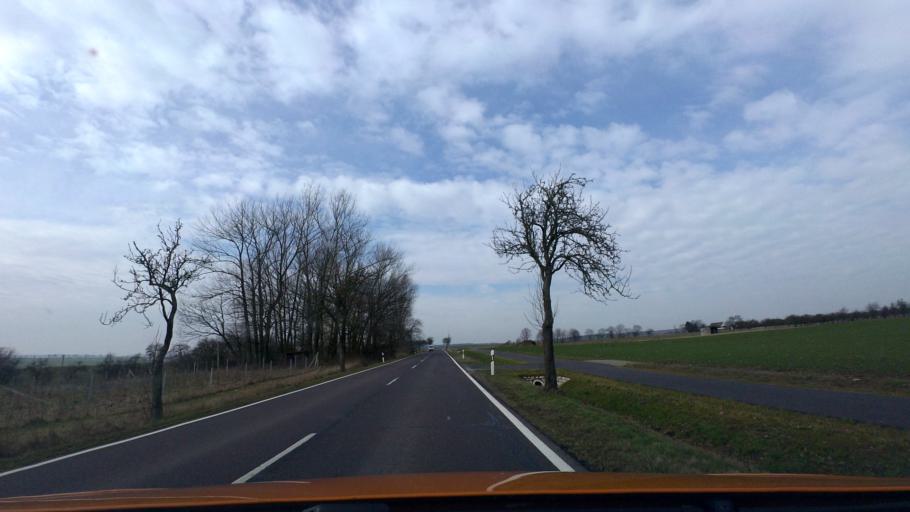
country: DE
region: Saxony-Anhalt
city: Erxleben
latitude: 52.2205
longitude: 11.2264
